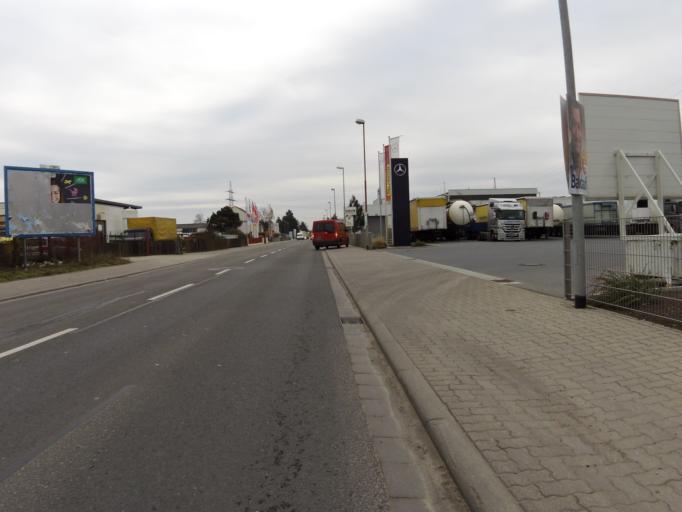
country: DE
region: Rheinland-Pfalz
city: Frankenthal
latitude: 49.5507
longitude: 8.3421
